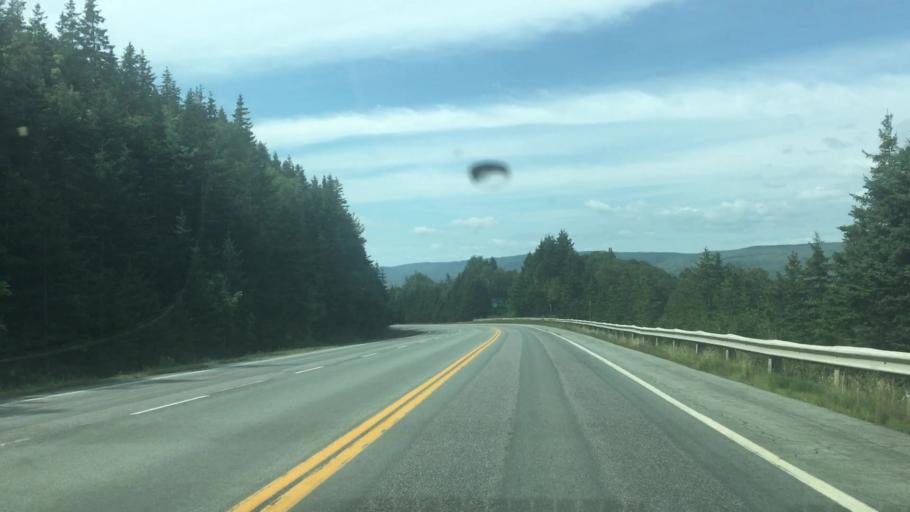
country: CA
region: Nova Scotia
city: Sydney Mines
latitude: 46.2456
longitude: -60.5560
